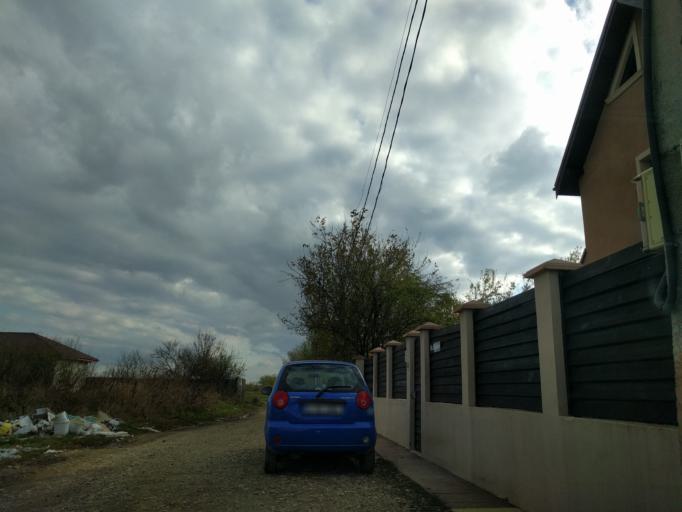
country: RO
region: Ilfov
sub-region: Comuna Branesti
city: Branesti
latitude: 44.4526
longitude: 26.3474
